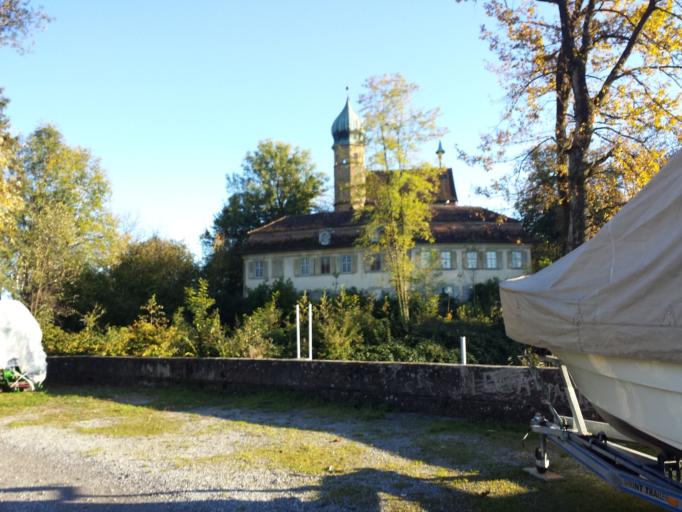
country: CH
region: Thurgau
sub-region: Arbon District
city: Egnach
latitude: 47.5487
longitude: 9.3826
